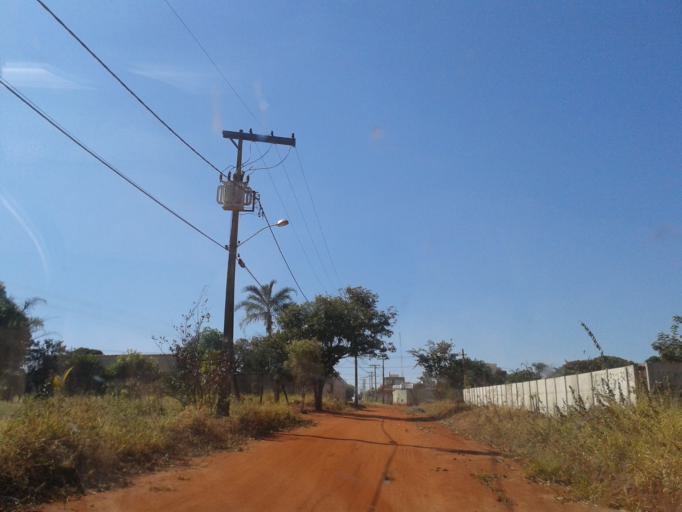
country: BR
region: Minas Gerais
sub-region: Ituiutaba
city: Ituiutaba
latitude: -18.9974
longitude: -49.4595
